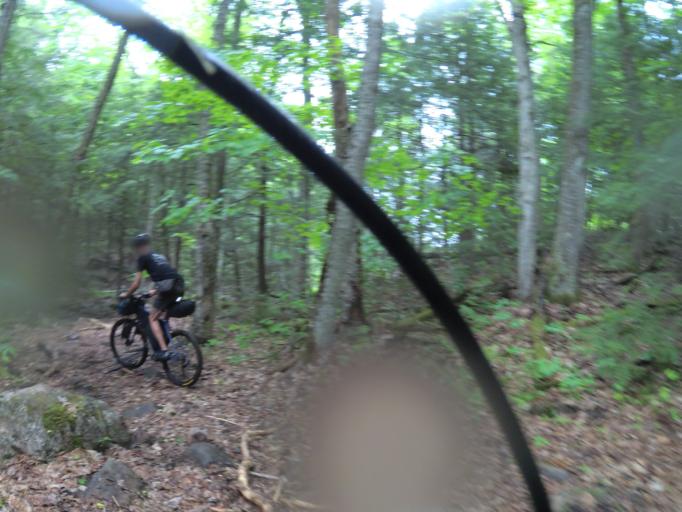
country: CA
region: Ontario
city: Renfrew
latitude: 45.0784
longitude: -76.8961
